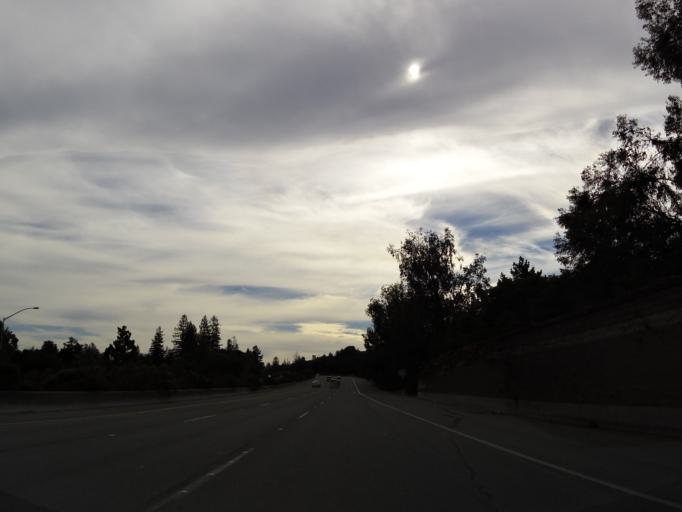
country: US
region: California
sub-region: Santa Clara County
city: Loyola
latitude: 37.3512
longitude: -122.1057
